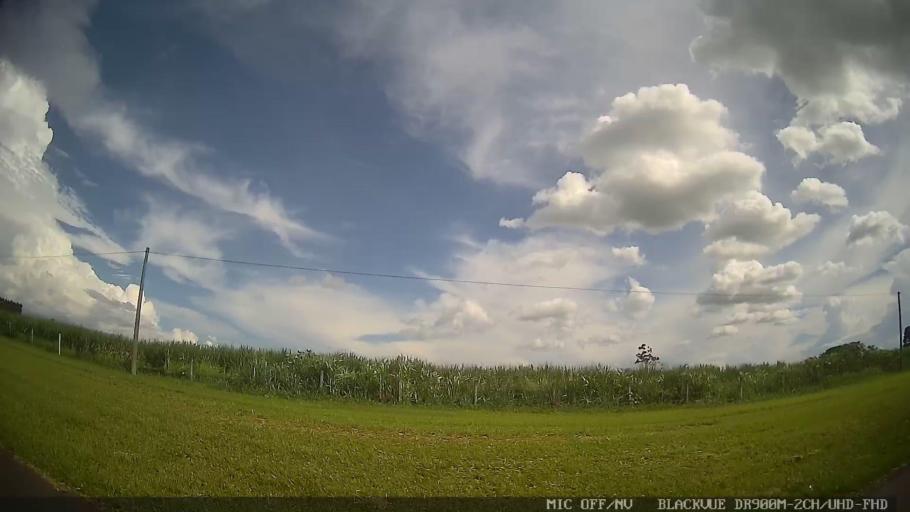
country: BR
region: Sao Paulo
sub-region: Laranjal Paulista
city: Laranjal Paulista
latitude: -23.0436
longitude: -47.9116
